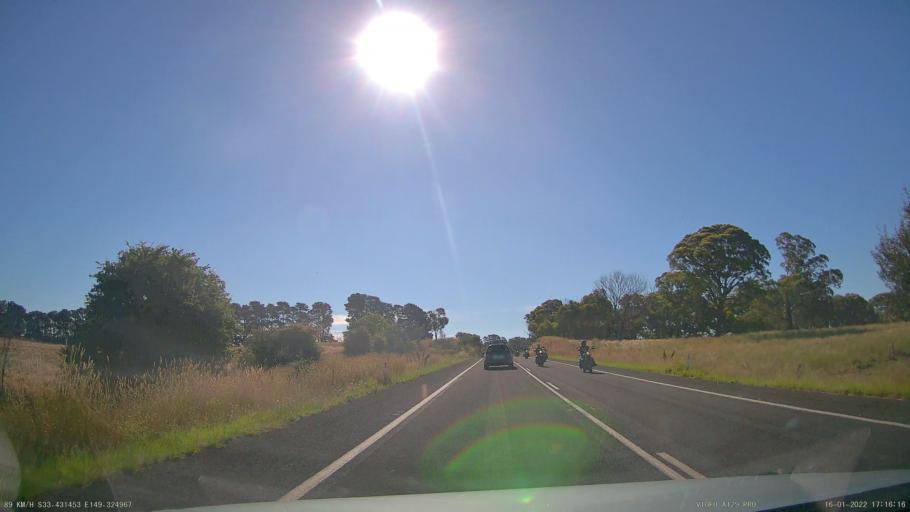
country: AU
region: New South Wales
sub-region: Blayney
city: Blayney
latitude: -33.4315
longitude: 149.3248
